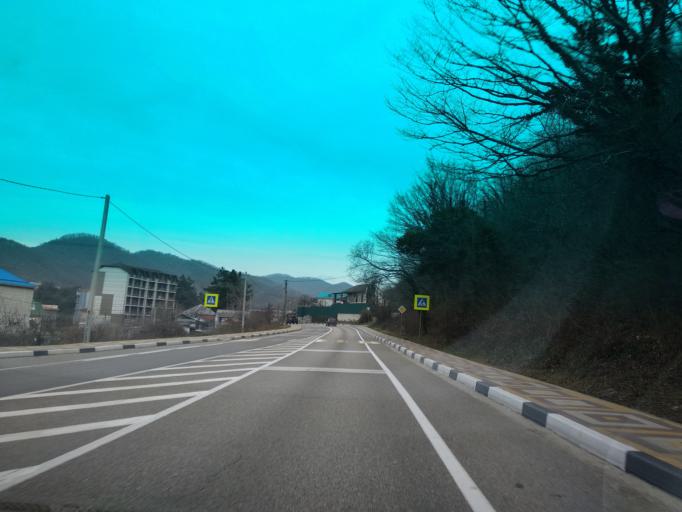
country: RU
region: Krasnodarskiy
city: Ol'ginka
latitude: 44.1953
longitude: 38.8918
